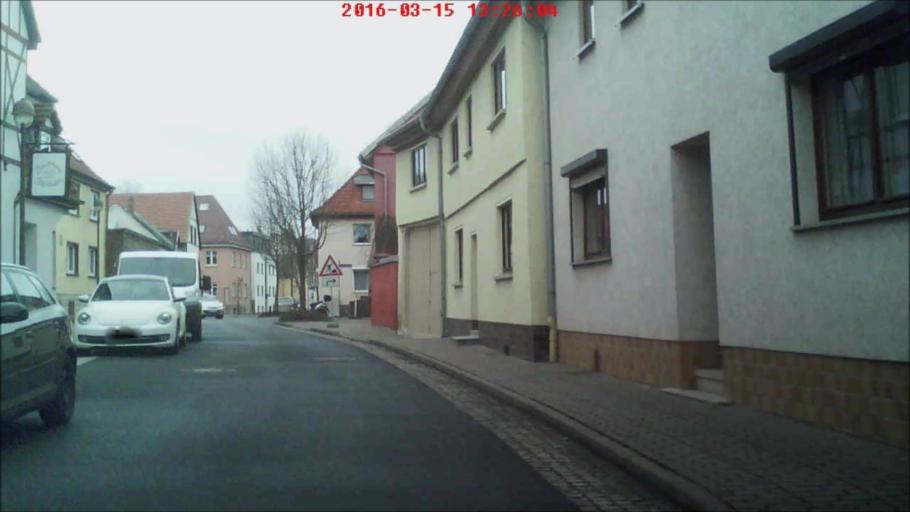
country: DE
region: Thuringia
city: Ingersleben
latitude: 50.9355
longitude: 10.9916
